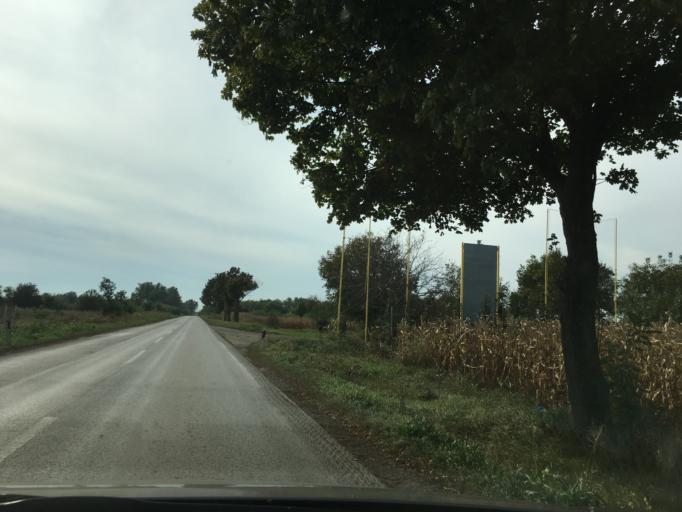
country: RS
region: Autonomna Pokrajina Vojvodina
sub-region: Juznobacki Okrug
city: Temerin
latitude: 45.4433
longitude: 19.9030
